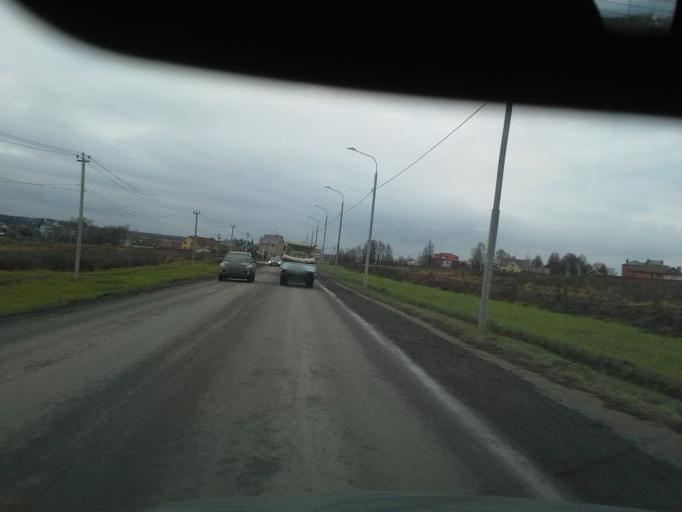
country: RU
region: Moskovskaya
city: Kommunarka
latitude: 55.5580
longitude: 37.4245
